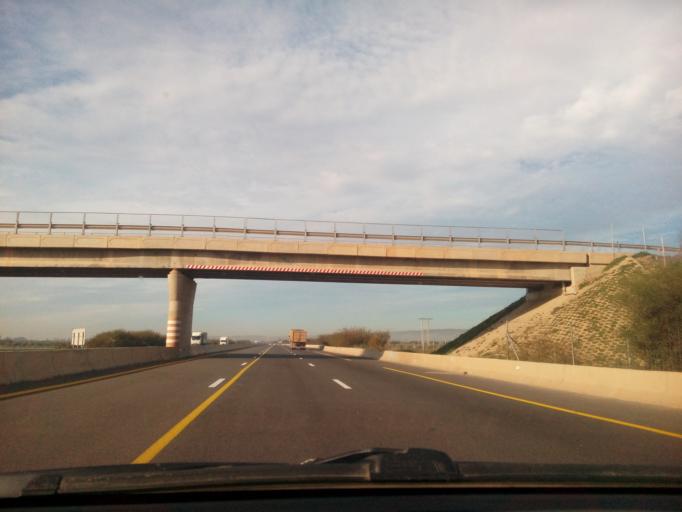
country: DZ
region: Mascara
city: Sig
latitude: 35.5811
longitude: -0.2391
